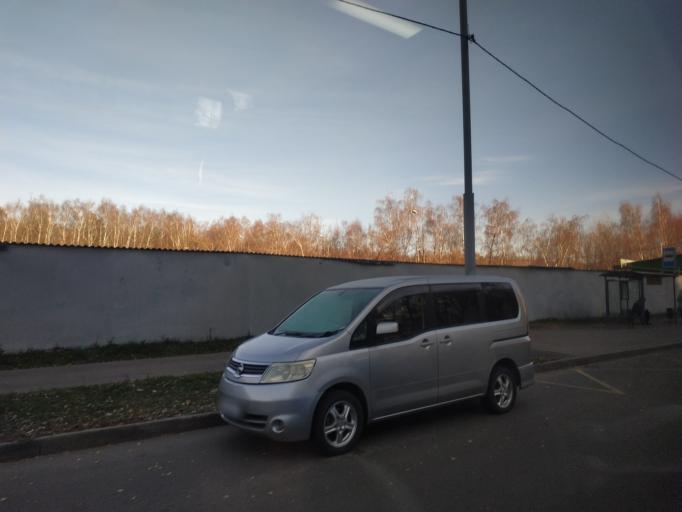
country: RU
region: Moscow
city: Biryulevo
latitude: 55.5857
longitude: 37.6880
